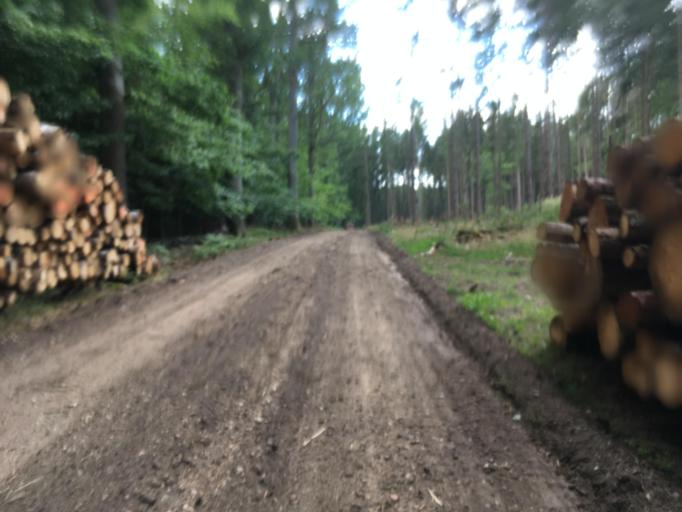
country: DE
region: Brandenburg
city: Joachimsthal
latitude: 52.9207
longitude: 13.7469
